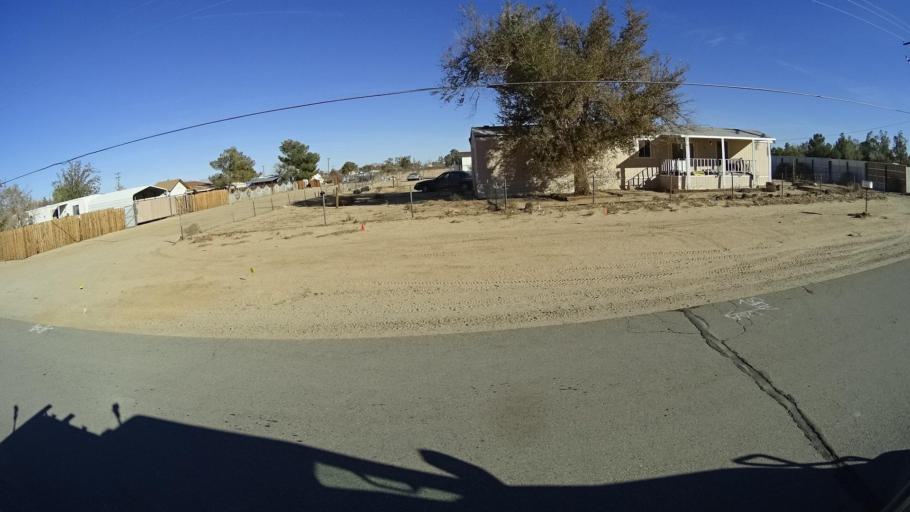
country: US
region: California
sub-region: Kern County
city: China Lake Acres
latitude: 35.6418
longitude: -117.7678
